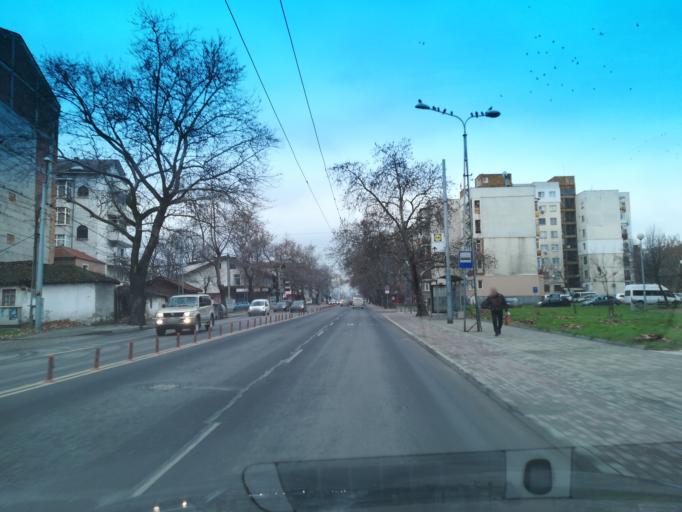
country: BG
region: Plovdiv
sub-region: Obshtina Plovdiv
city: Plovdiv
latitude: 42.1512
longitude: 24.7632
